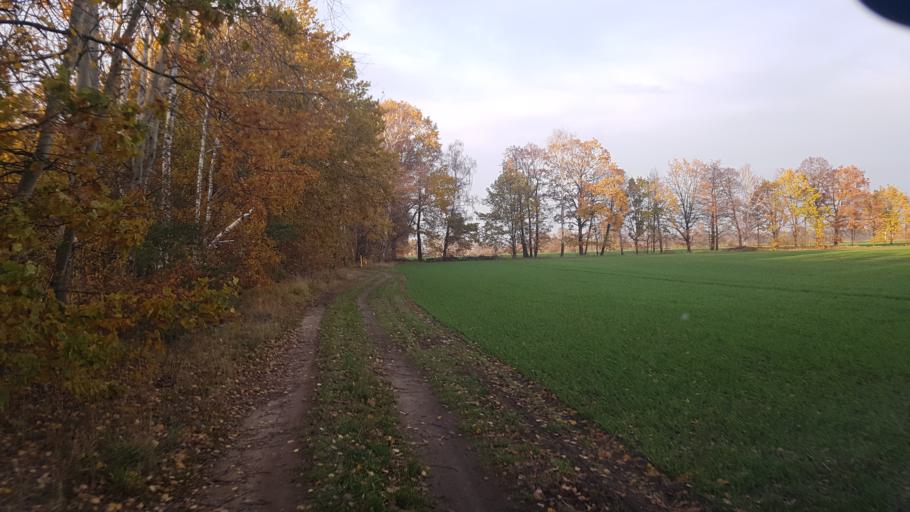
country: DE
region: Brandenburg
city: Schonewalde
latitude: 51.6439
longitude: 13.6002
